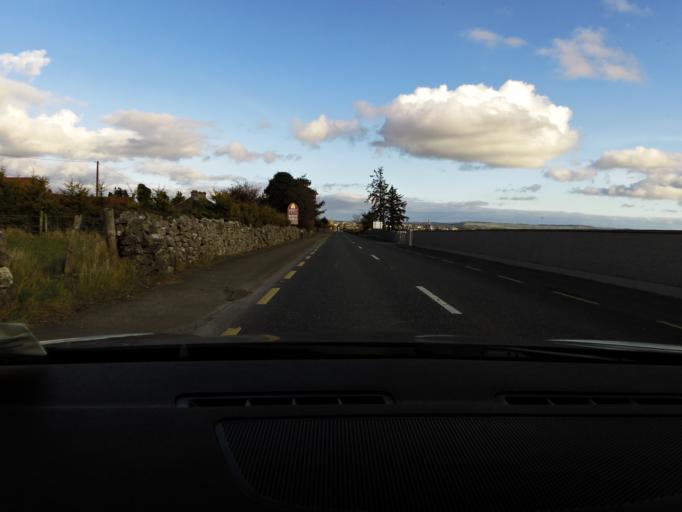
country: IE
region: Connaught
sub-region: Roscommon
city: Roscommon
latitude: 53.6462
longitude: -8.2206
